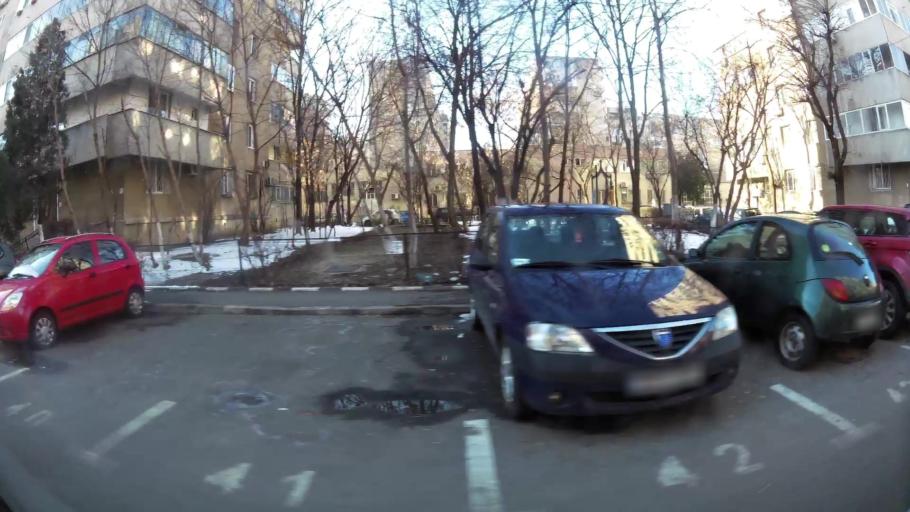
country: RO
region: Bucuresti
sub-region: Municipiul Bucuresti
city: Bucharest
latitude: 44.4125
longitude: 26.1109
